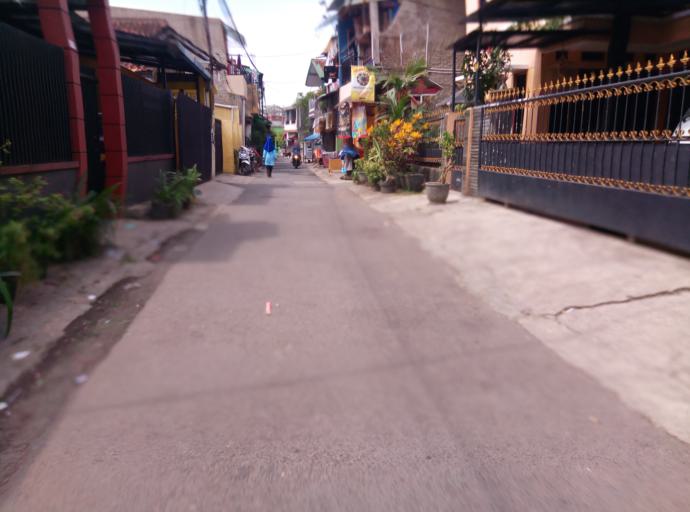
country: ID
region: West Java
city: Bandung
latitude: -6.9280
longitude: 107.6479
